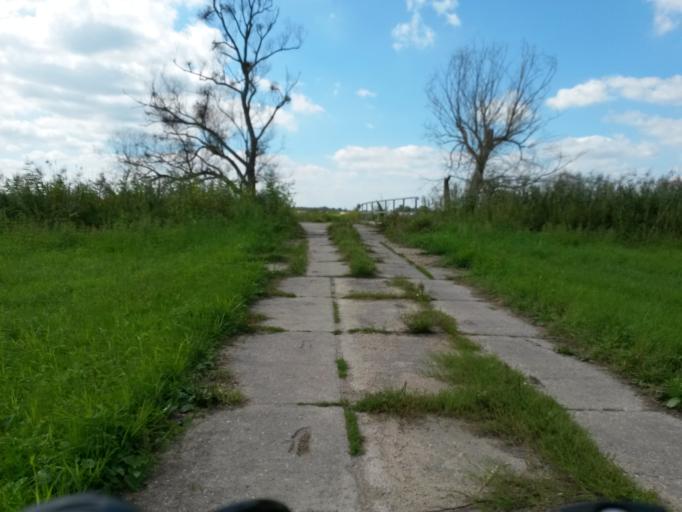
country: DE
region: Brandenburg
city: Meyenburg
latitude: 53.0124
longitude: 14.2490
